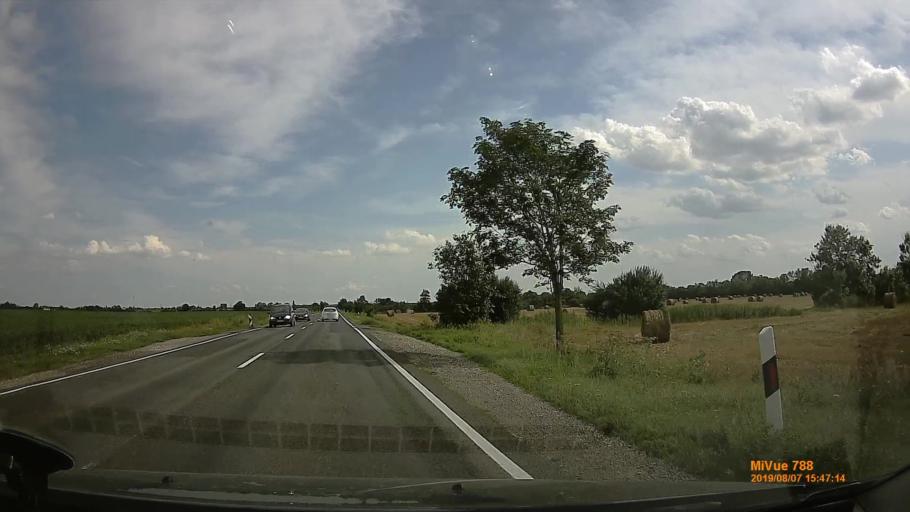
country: HU
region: Vas
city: Jak
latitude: 47.1741
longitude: 16.6253
